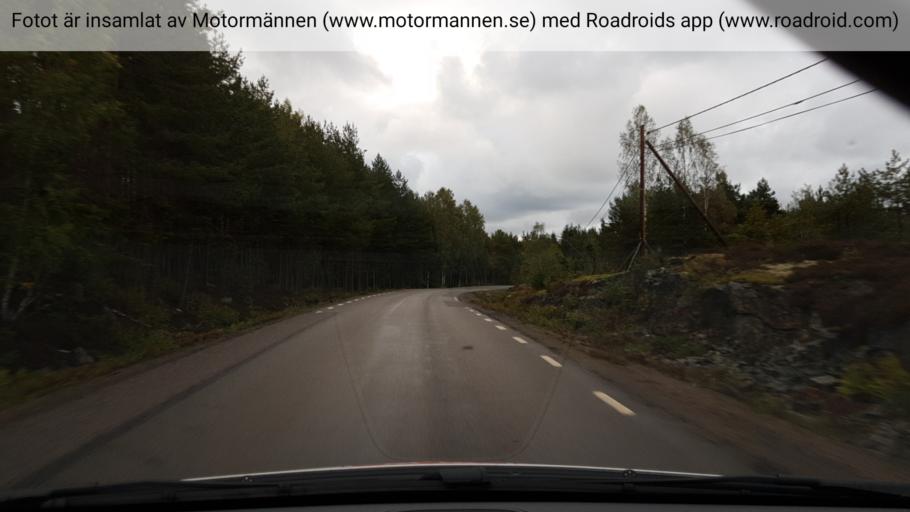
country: SE
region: Vaermland
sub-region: Saffle Kommun
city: Saeffle
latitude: 58.9349
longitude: 13.1924
